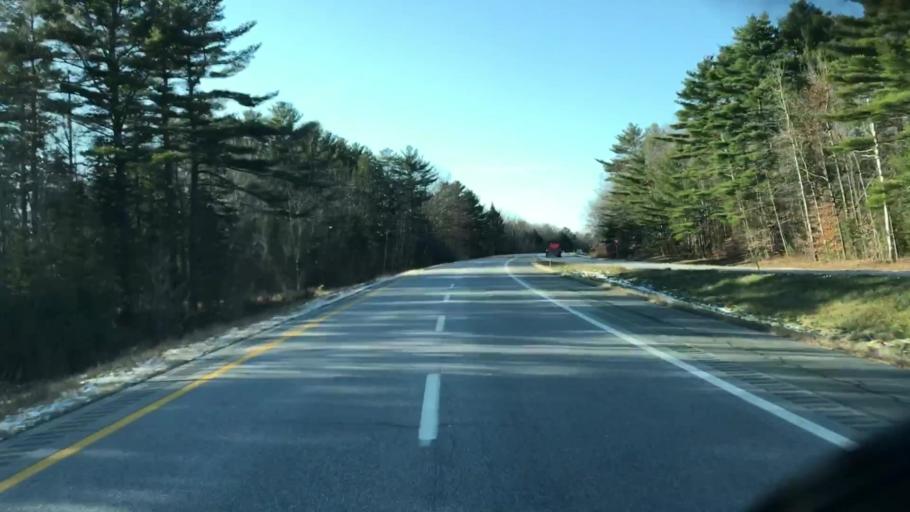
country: US
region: Maine
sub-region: Penobscot County
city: Hermon
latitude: 44.7594
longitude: -68.9775
